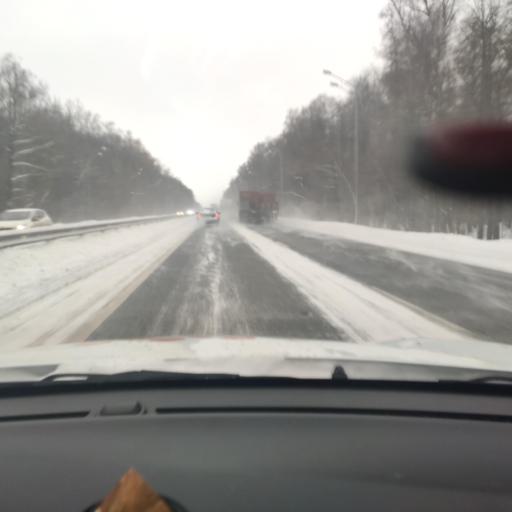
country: RU
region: Tatarstan
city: Osinovo
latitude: 55.8451
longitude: 48.8523
